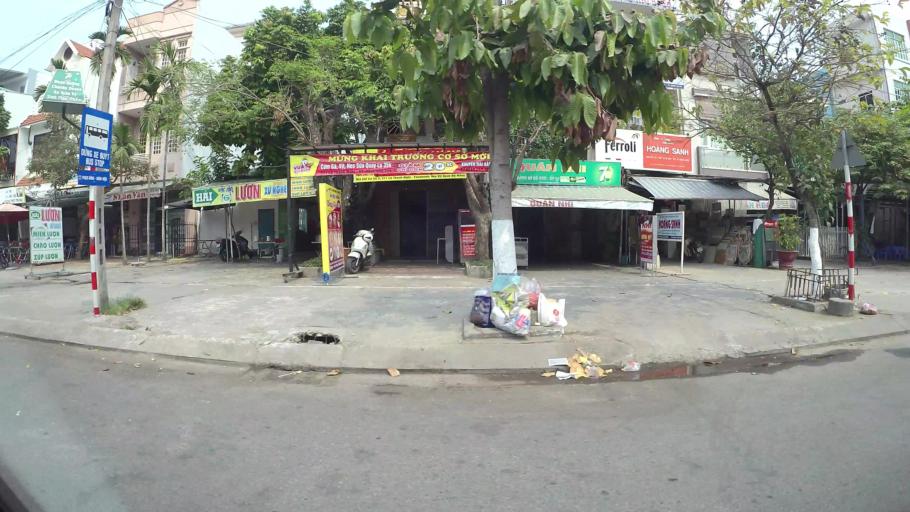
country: VN
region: Da Nang
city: Cam Le
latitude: 16.0372
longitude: 108.2183
